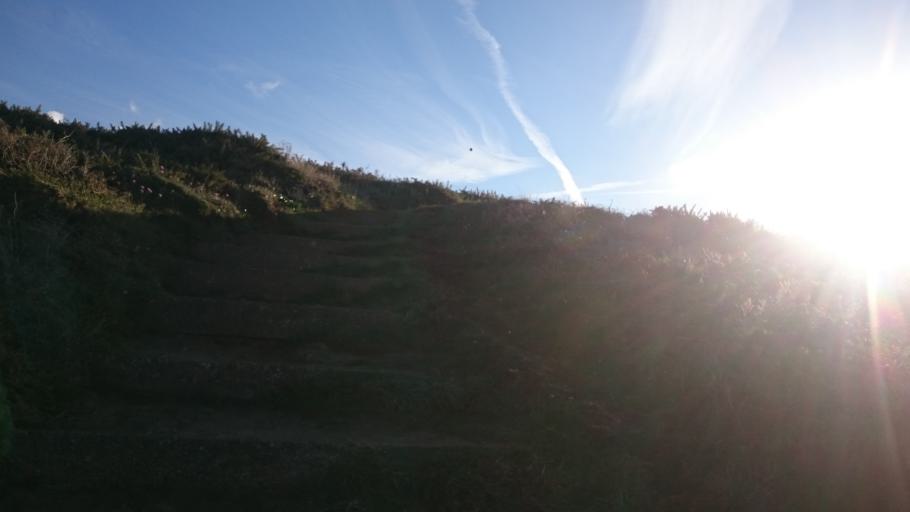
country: GG
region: St Peter Port
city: Saint Peter Port
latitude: 49.4262
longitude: -2.6651
